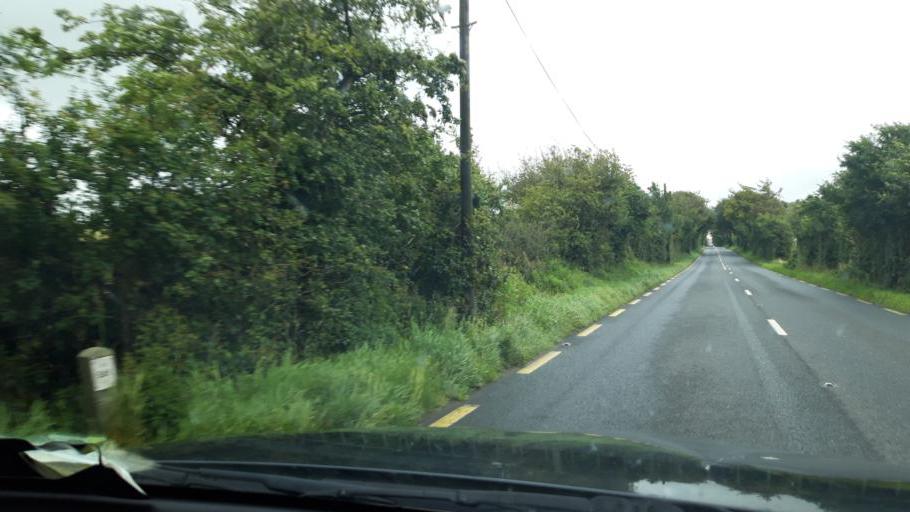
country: IE
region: Leinster
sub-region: Loch Garman
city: New Ross
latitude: 52.4332
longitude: -6.7812
